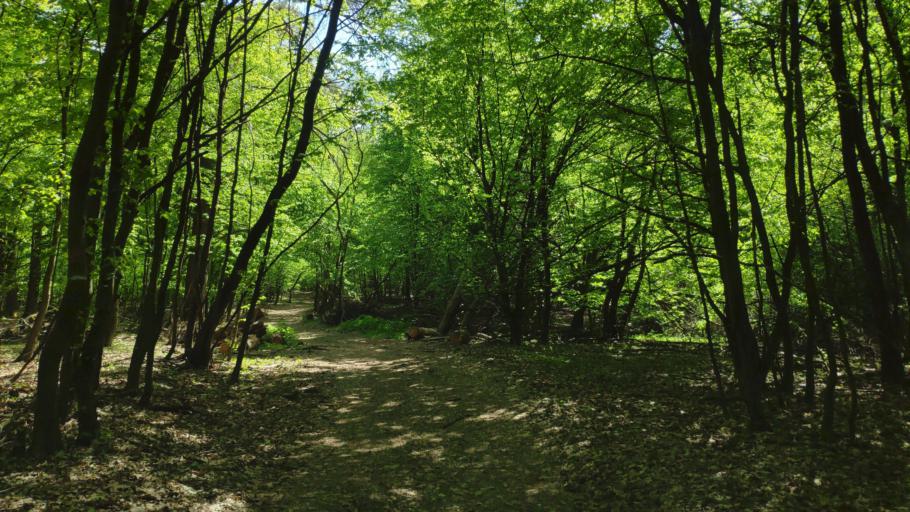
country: SK
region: Kosicky
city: Kosice
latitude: 48.6659
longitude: 21.4309
